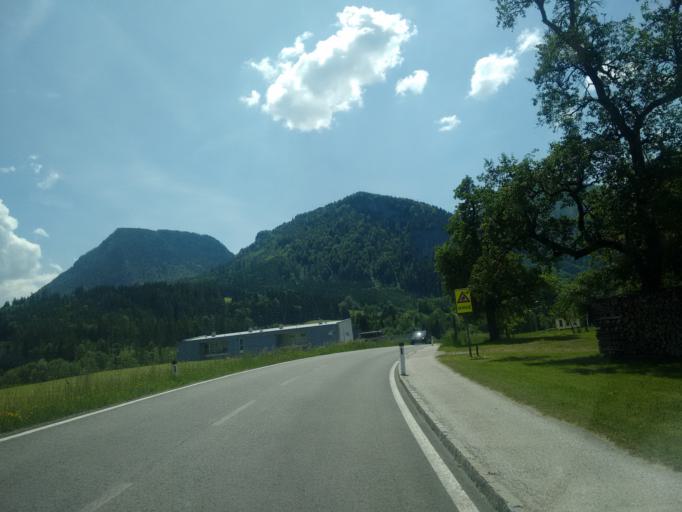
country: AT
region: Upper Austria
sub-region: Politischer Bezirk Kirchdorf an der Krems
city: Rossleithen
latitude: 47.7036
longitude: 14.2789
